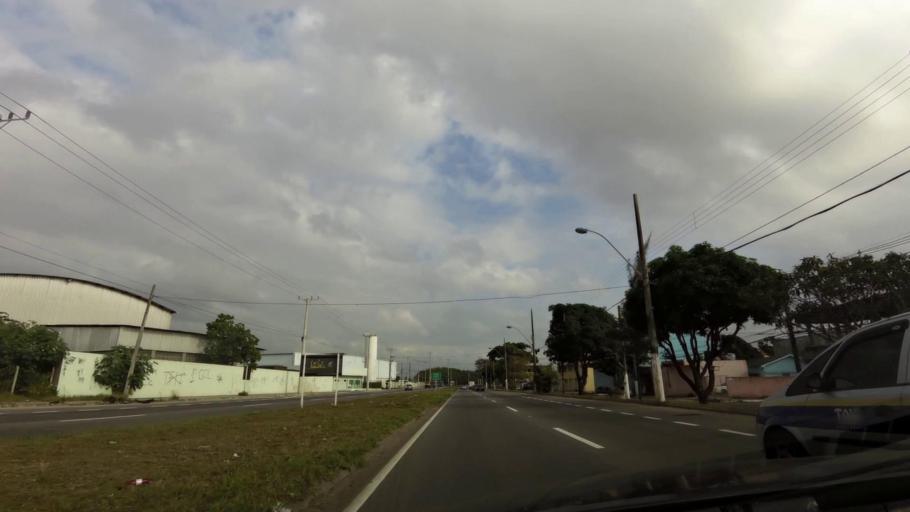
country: BR
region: Espirito Santo
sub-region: Vitoria
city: Vitoria
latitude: -20.3861
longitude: -40.3300
